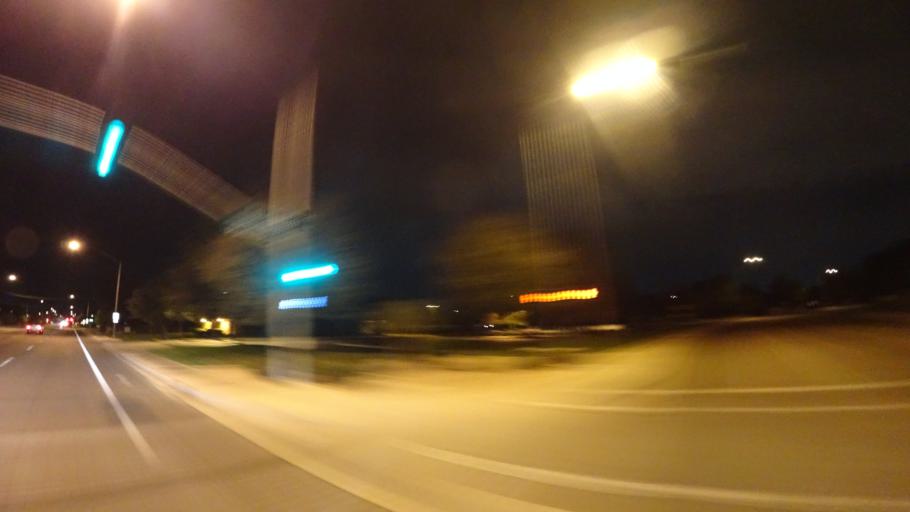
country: US
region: Arizona
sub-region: Maricopa County
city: Gilbert
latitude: 33.3993
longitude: -111.7713
